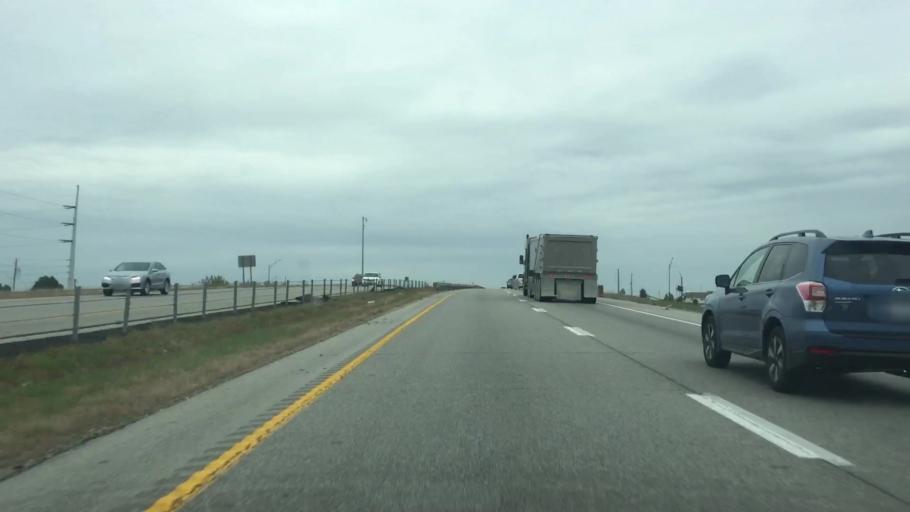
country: US
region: Missouri
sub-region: Jackson County
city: Lees Summit
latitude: 38.9243
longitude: -94.4035
